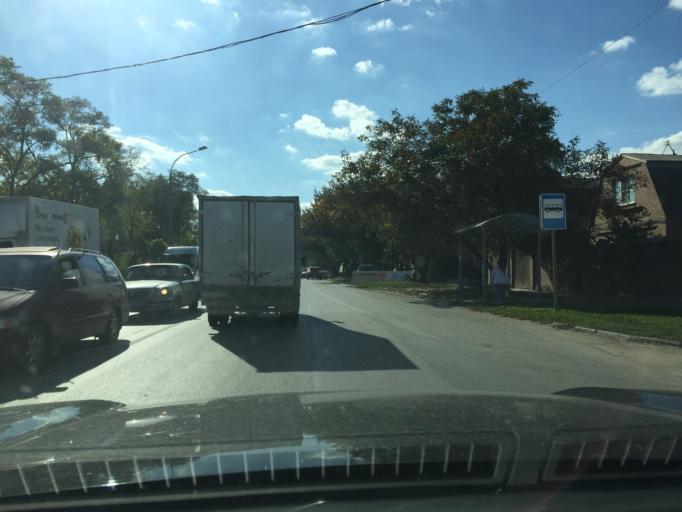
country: RU
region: Rostov
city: Rostov-na-Donu
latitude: 47.2419
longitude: 39.6417
